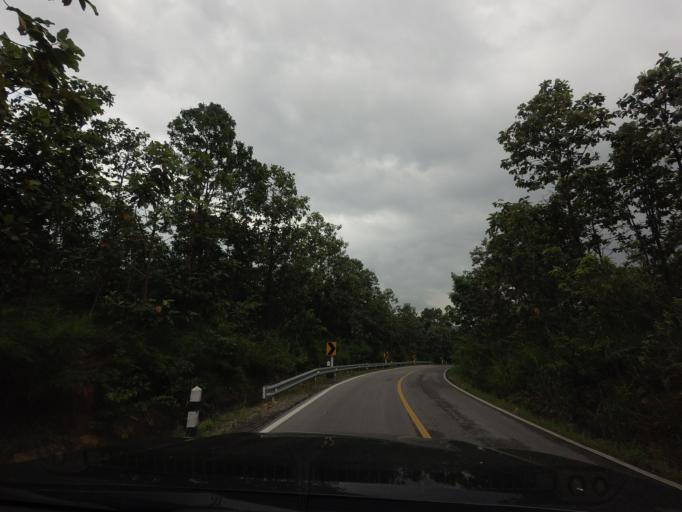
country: TH
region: Nong Khai
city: Sangkhom
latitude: 18.0303
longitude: 102.3417
